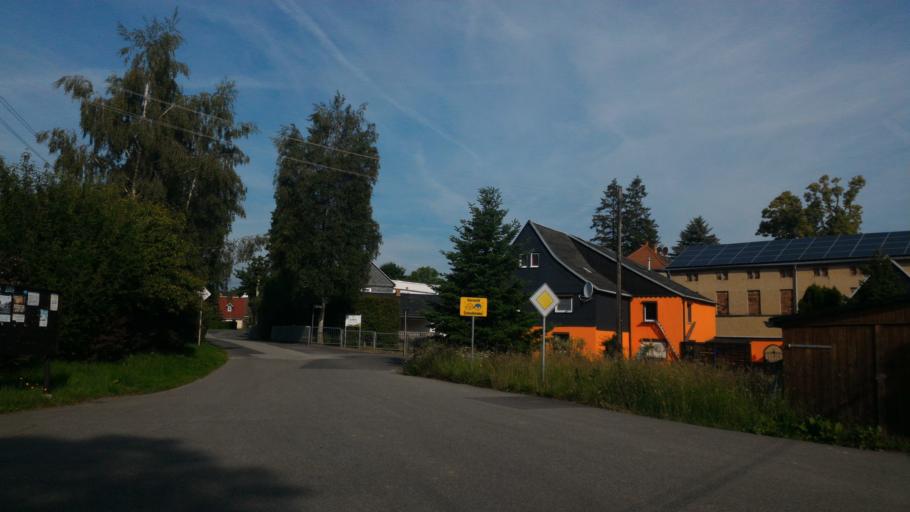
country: DE
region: Saxony
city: Leutersdorf
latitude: 50.9581
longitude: 14.6495
